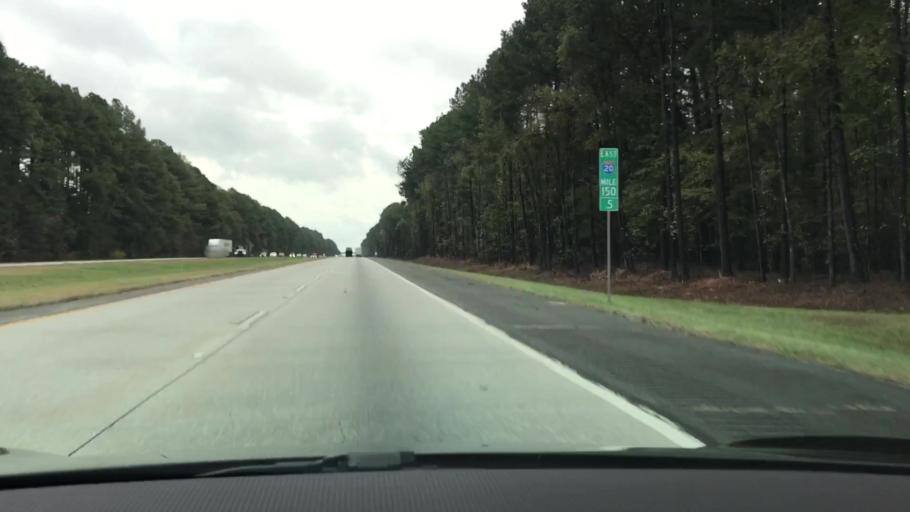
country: US
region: Georgia
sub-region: Taliaferro County
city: Crawfordville
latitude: 33.5189
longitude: -82.8642
